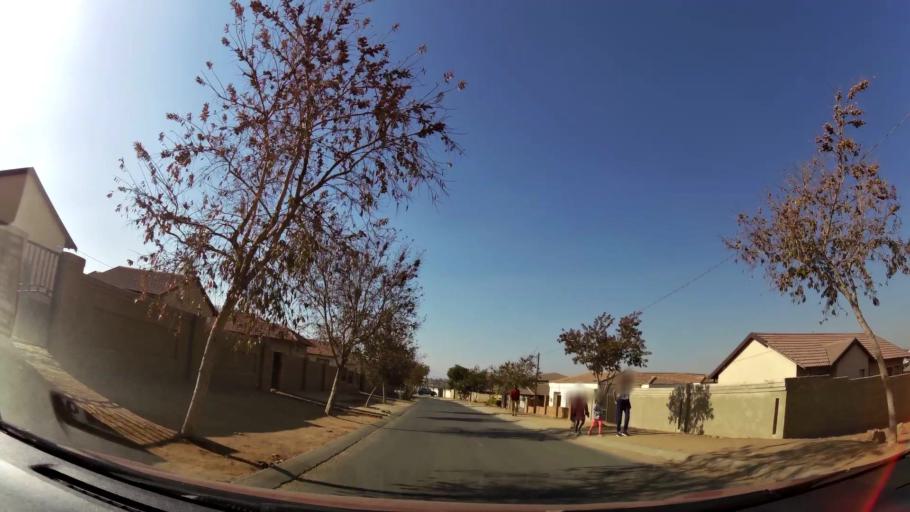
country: ZA
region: Gauteng
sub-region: West Rand District Municipality
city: Muldersdriseloop
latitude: -26.0383
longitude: 27.9136
